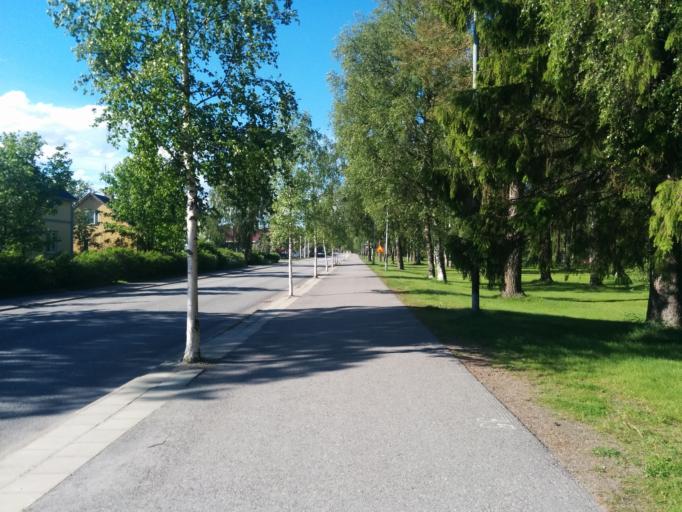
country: SE
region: Vaesterbotten
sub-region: Umea Kommun
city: Hoernefors
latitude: 63.6250
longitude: 19.9086
